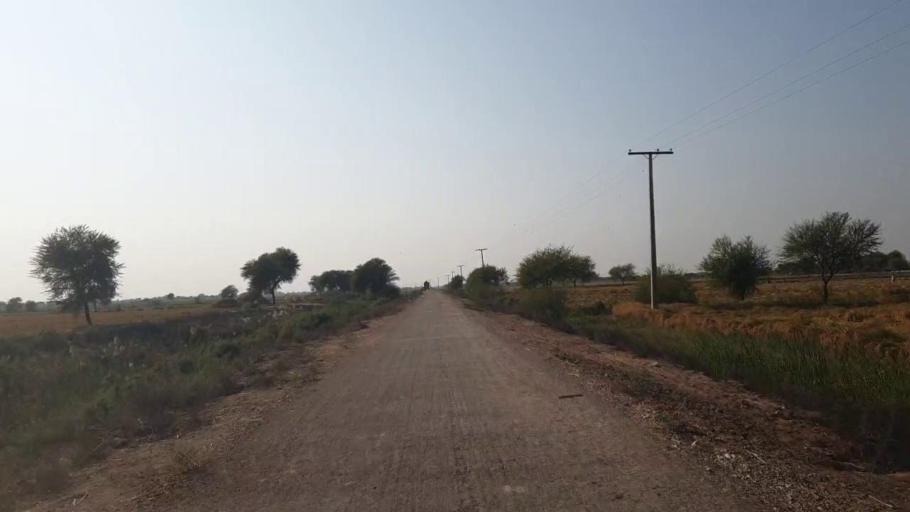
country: PK
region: Sindh
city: Kario
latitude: 24.8920
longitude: 68.6389
